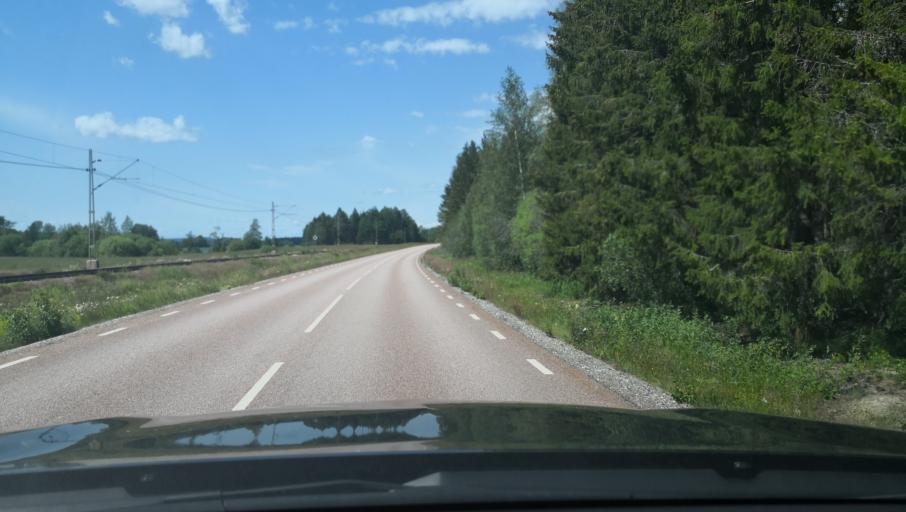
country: SE
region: Vaestmanland
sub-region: Surahammars Kommun
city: Ramnas
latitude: 59.8506
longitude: 16.0994
